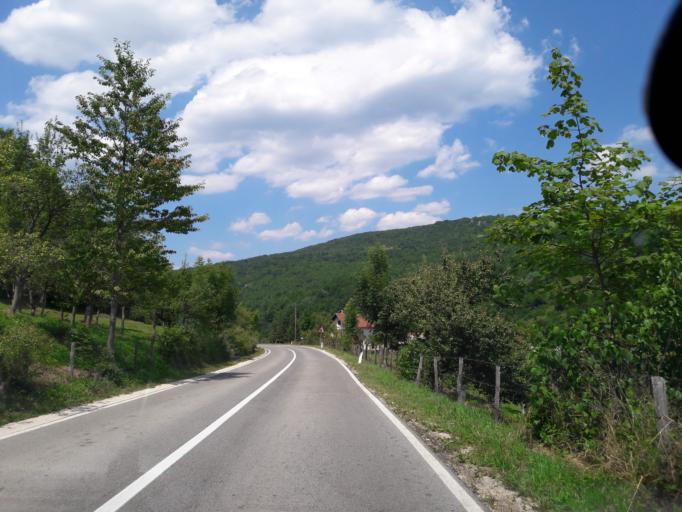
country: BA
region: Republika Srpska
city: Sipovo
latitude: 44.2154
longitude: 17.1245
